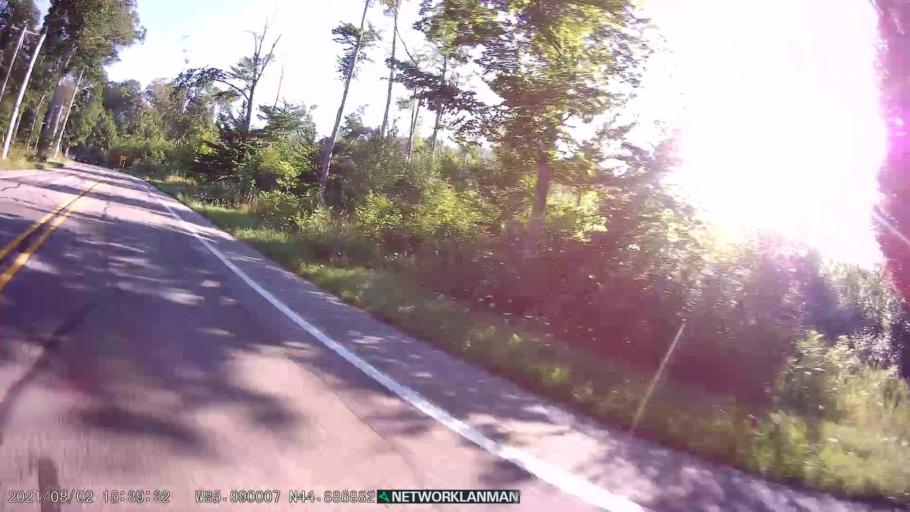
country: US
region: Michigan
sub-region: Leelanau County
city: Leland
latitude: 44.8867
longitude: -85.9900
